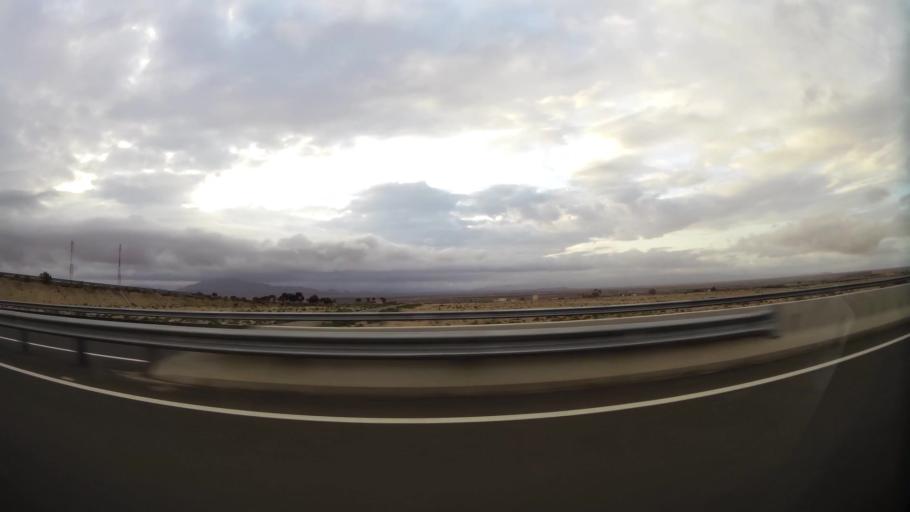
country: MA
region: Taza-Al Hoceima-Taounate
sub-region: Taza
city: Guercif
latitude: 34.4081
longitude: -3.1707
